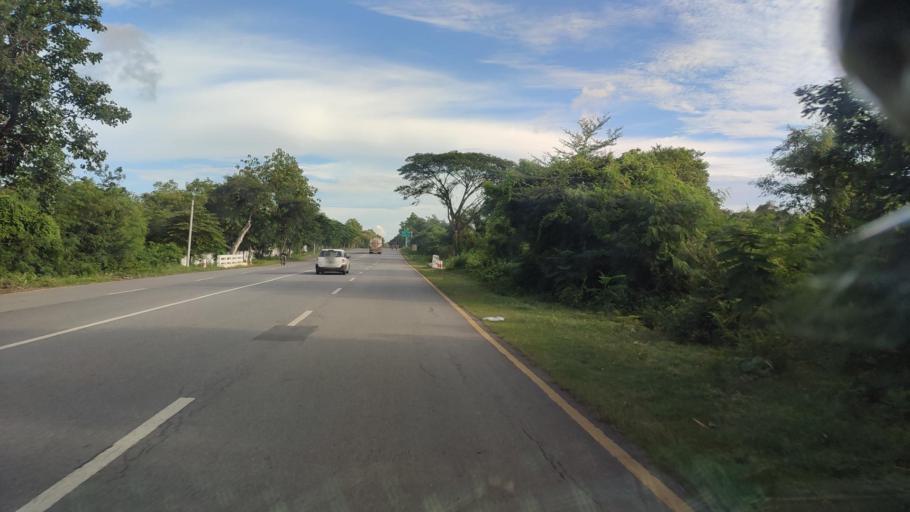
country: MM
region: Mandalay
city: Yamethin
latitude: 20.1616
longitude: 96.1905
